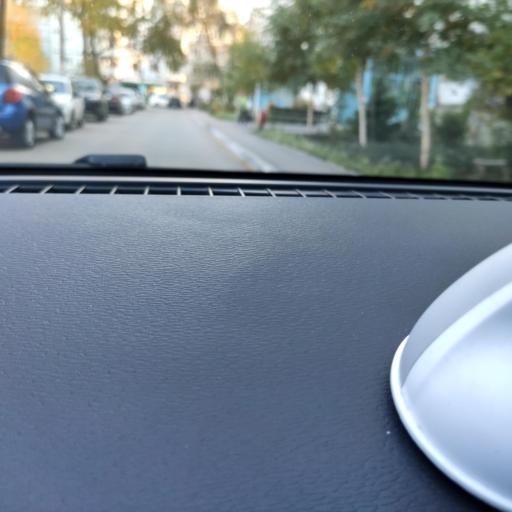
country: RU
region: Samara
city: Samara
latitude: 53.2621
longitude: 50.2266
